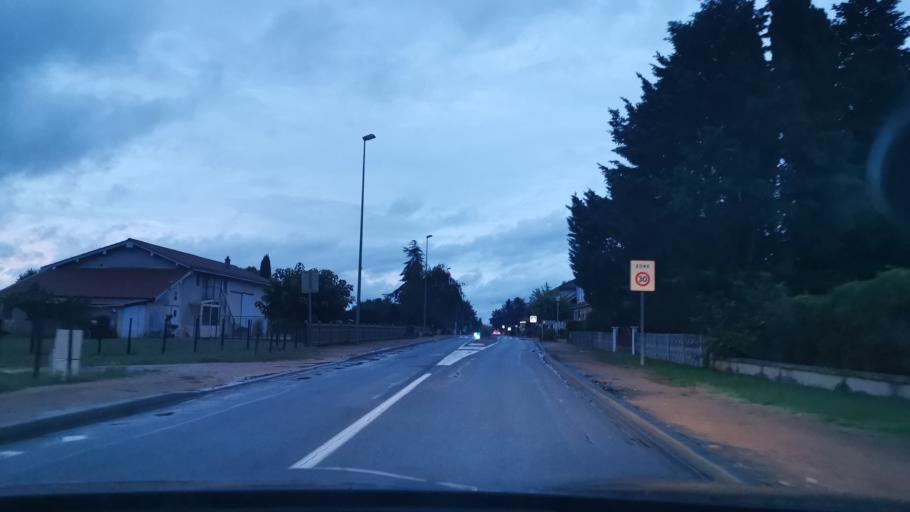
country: FR
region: Rhone-Alpes
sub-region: Departement de l'Ain
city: Crottet
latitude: 46.2940
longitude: 4.9166
